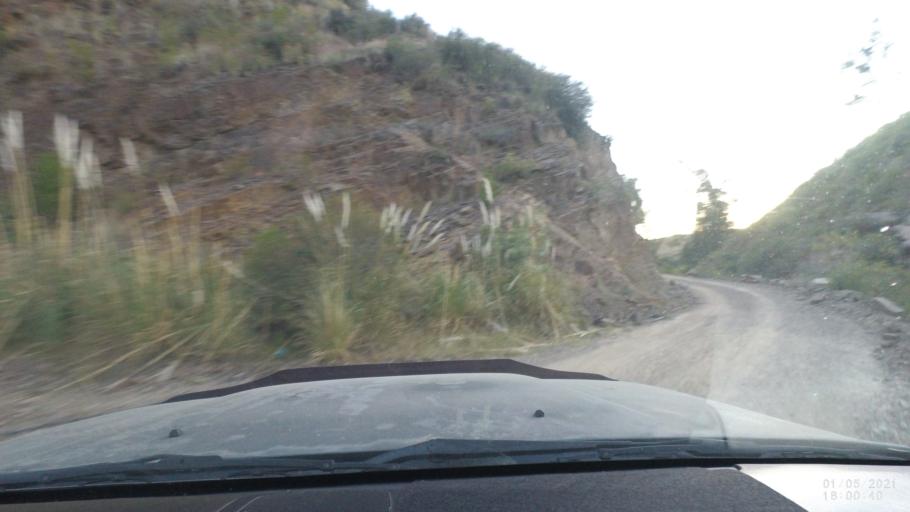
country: BO
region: Cochabamba
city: Capinota
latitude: -17.6846
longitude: -66.1686
